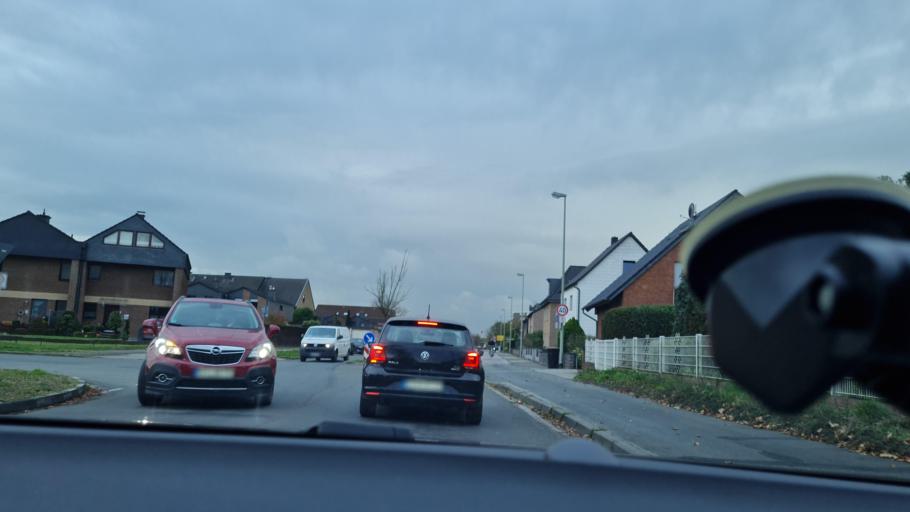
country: DE
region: North Rhine-Westphalia
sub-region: Regierungsbezirk Dusseldorf
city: Voerde
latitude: 51.6223
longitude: 6.6489
